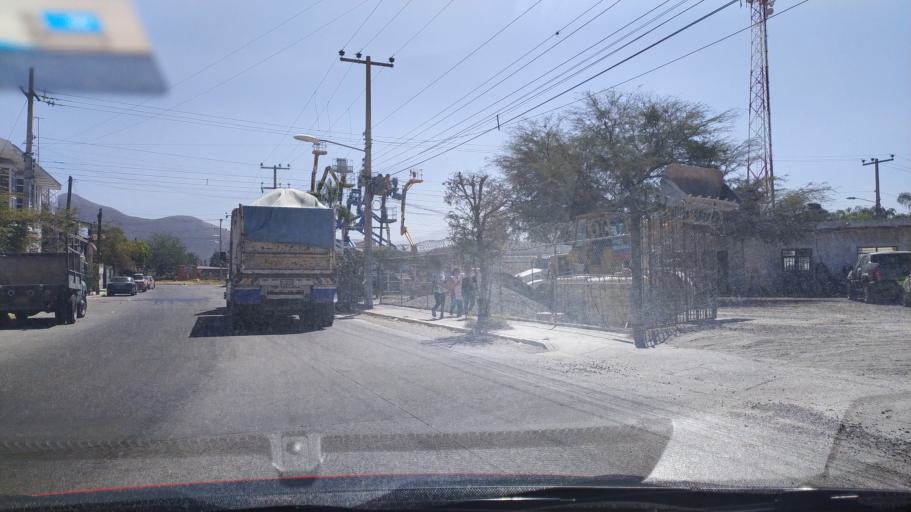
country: MX
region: Jalisco
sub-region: Tlajomulco de Zuniga
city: Santa Cruz de las Flores
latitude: 20.4884
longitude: -103.4940
